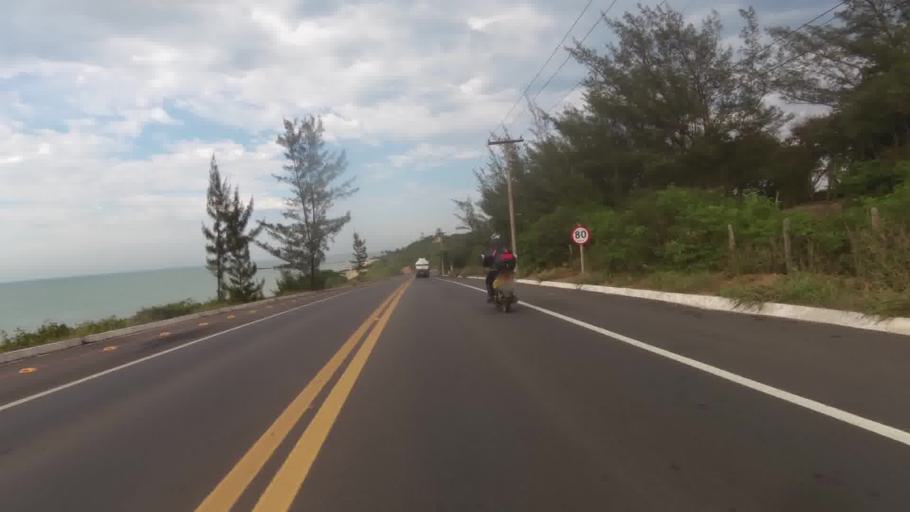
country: BR
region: Espirito Santo
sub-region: Piuma
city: Piuma
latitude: -20.8133
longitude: -40.6133
